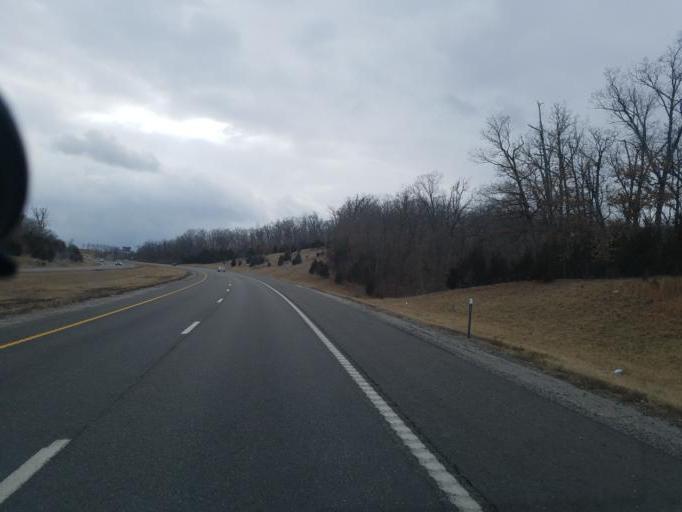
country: US
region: Missouri
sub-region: Boone County
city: Columbia
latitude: 38.9686
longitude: -92.2931
